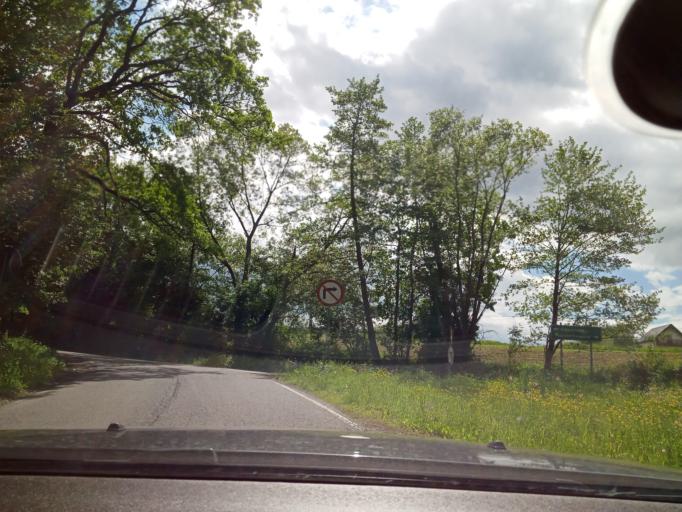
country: PL
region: Lesser Poland Voivodeship
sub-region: Powiat bochenski
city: Lapanow
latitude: 49.8612
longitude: 20.2500
